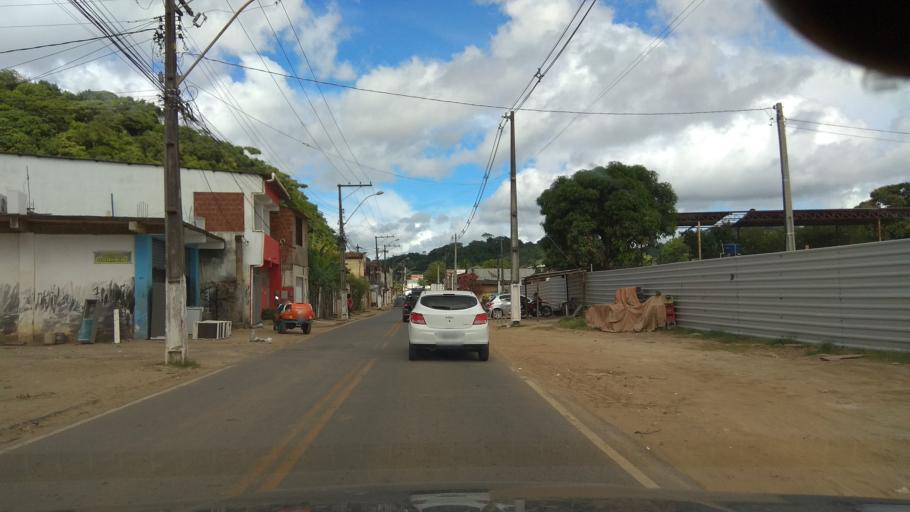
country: BR
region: Bahia
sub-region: Ilheus
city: Ilheus
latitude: -14.7896
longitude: -39.0608
